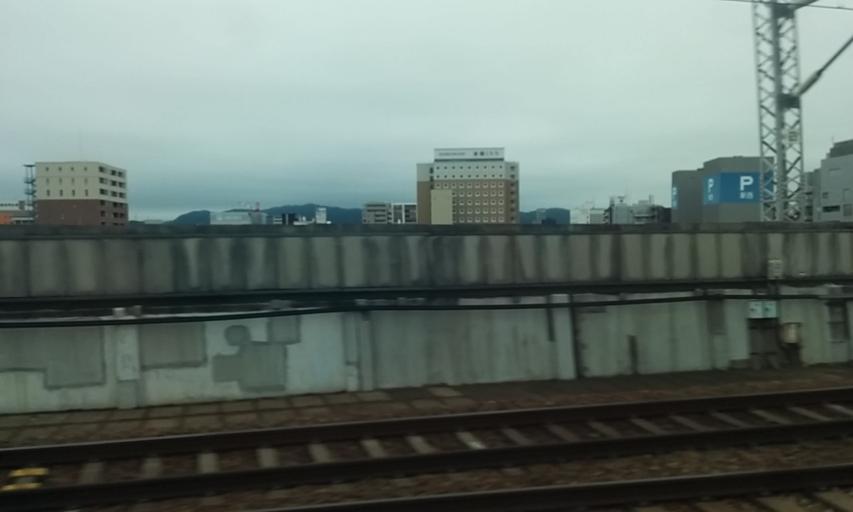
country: JP
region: Hyogo
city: Himeji
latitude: 34.8268
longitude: 134.6867
